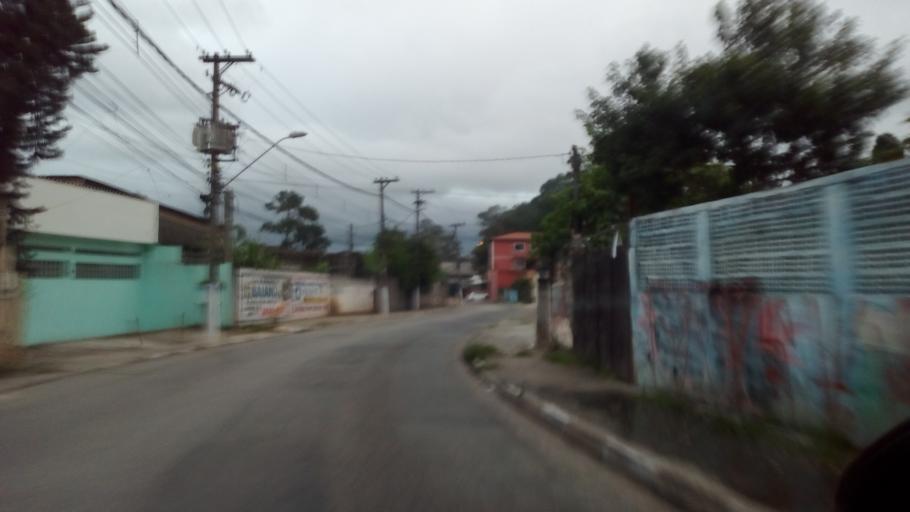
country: BR
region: Sao Paulo
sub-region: Itaquaquecetuba
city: Itaquaquecetuba
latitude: -23.4284
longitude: -46.4034
